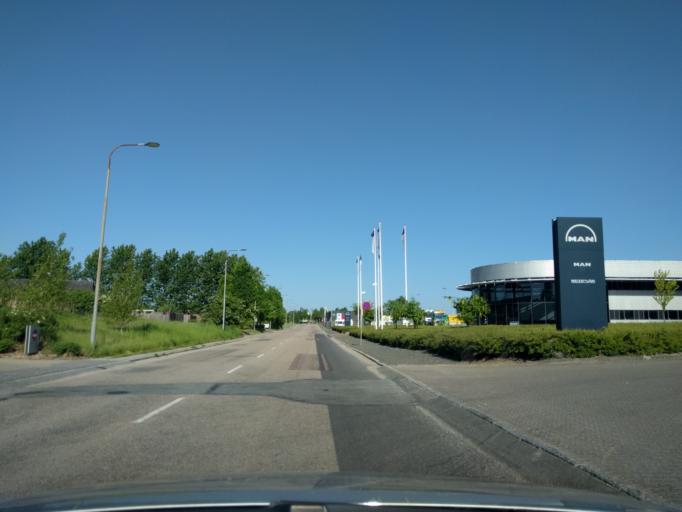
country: DK
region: South Denmark
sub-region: Odense Kommune
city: Bellinge
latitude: 55.3553
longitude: 10.3333
